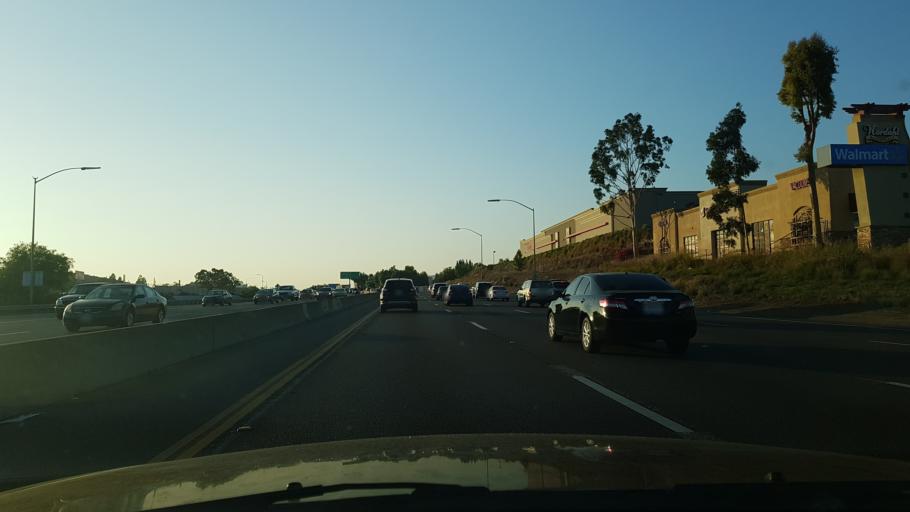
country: US
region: California
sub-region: San Diego County
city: Escondido
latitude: 33.1334
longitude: -117.1244
